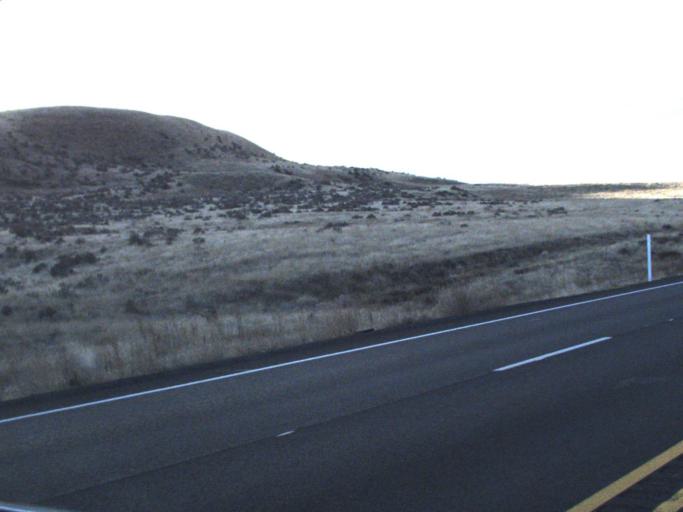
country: US
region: Washington
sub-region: Walla Walla County
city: Burbank
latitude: 46.0699
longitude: -118.7690
